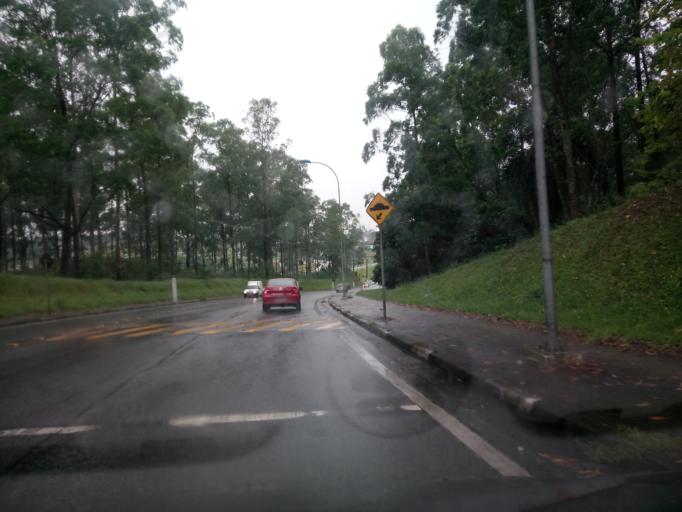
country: BR
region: Sao Paulo
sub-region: Sao Bernardo Do Campo
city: Sao Bernardo do Campo
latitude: -23.7599
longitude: -46.5947
